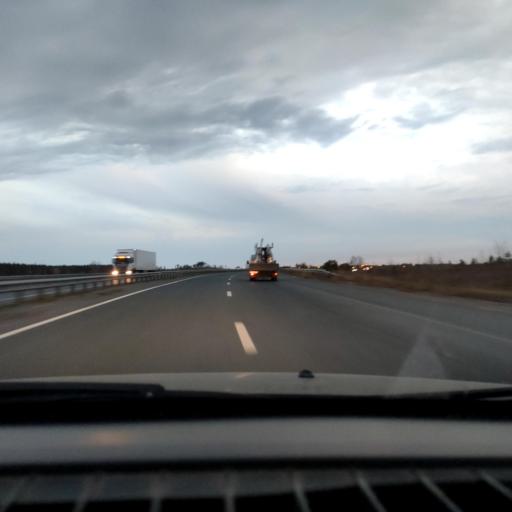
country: RU
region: Samara
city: Zhigulevsk
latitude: 53.5161
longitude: 49.5363
